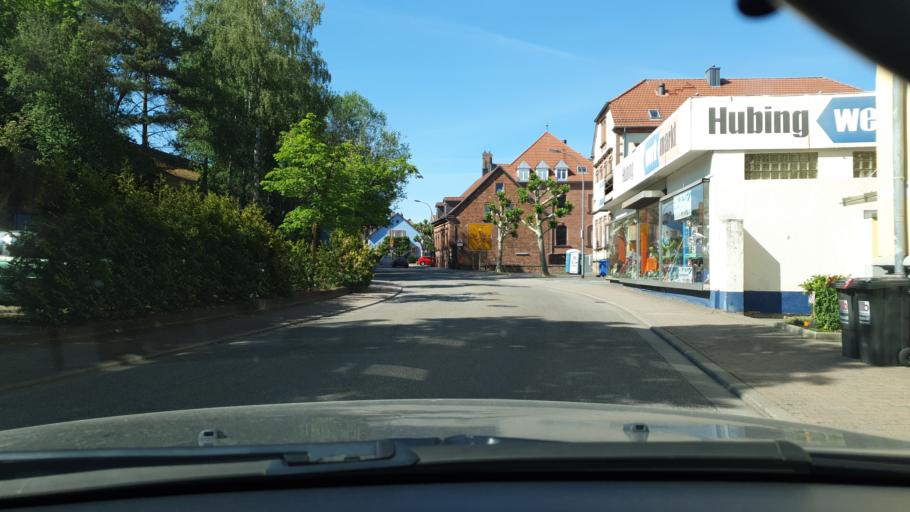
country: DE
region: Rheinland-Pfalz
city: Otterberg
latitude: 49.4994
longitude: 7.7730
